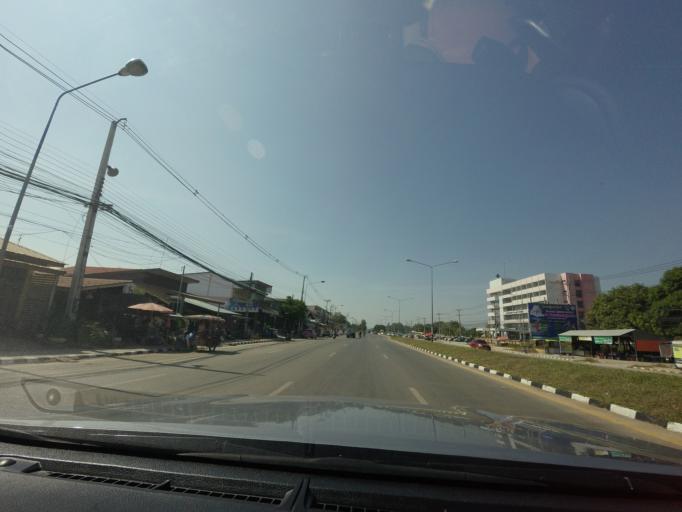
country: TH
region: Sukhothai
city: Sukhothai
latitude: 17.0099
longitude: 99.7974
